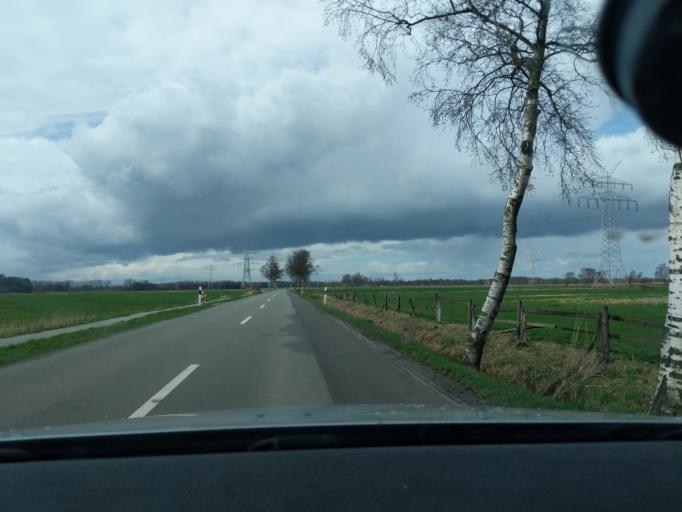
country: DE
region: Lower Saxony
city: Stade
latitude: 53.6186
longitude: 9.4530
